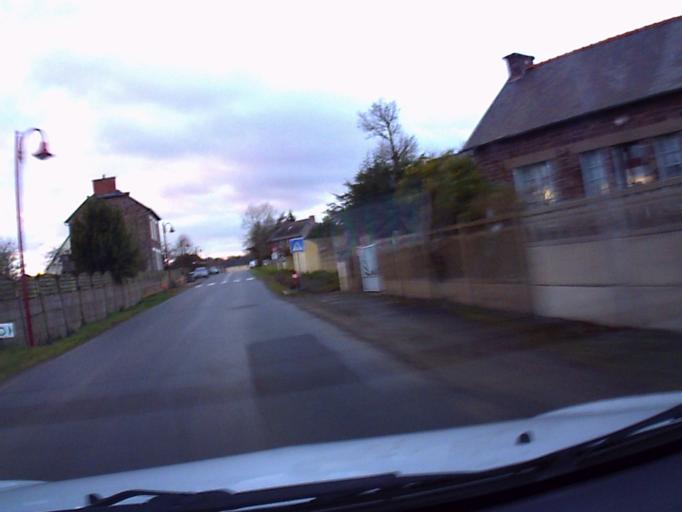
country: FR
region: Brittany
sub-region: Departement d'Ille-et-Vilaine
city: Iffendic
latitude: 48.1124
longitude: -2.0631
